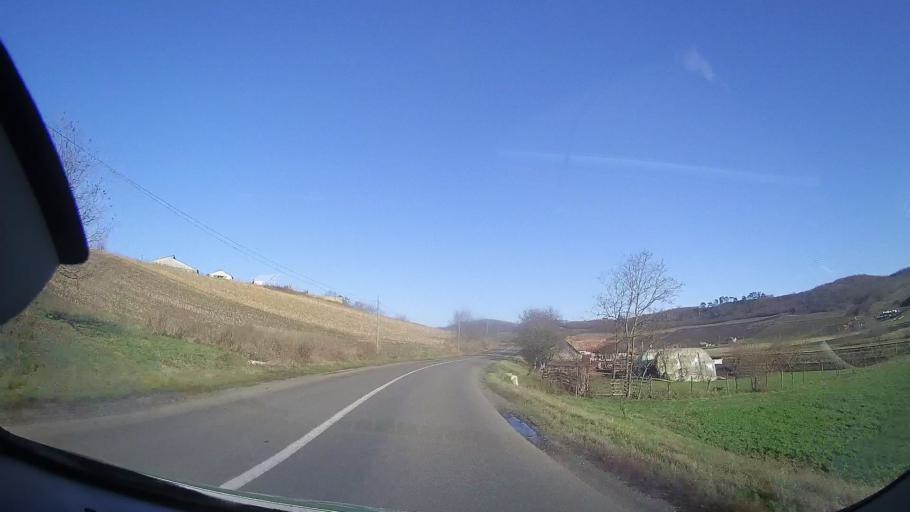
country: RO
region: Mures
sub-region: Comuna Sarmasu
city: Sarmasu
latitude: 46.7736
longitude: 24.1987
